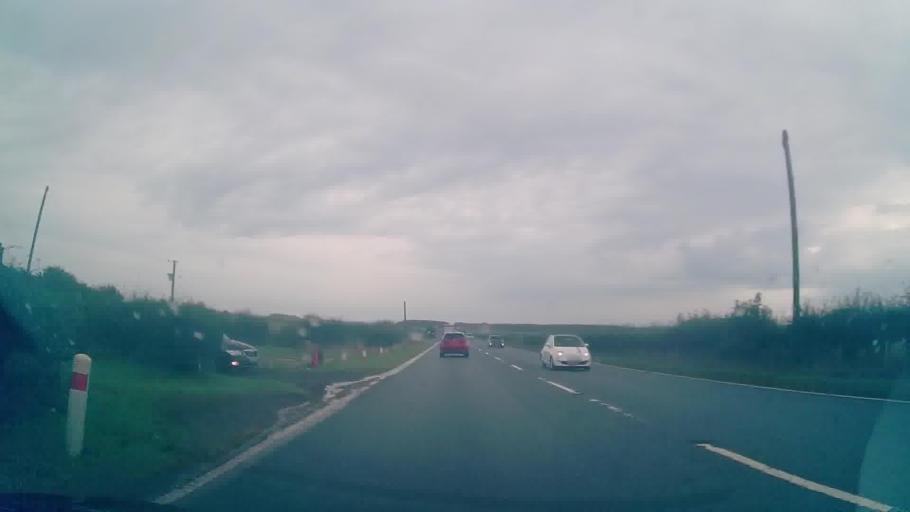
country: GB
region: Scotland
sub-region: Dumfries and Galloway
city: Annan
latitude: 55.0063
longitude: -3.3283
